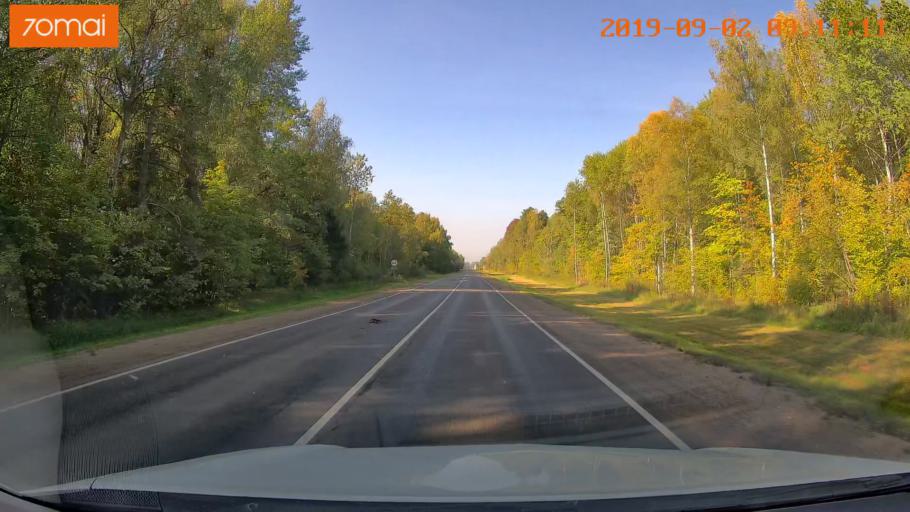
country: RU
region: Kaluga
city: Myatlevo
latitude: 54.8696
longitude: 35.5820
